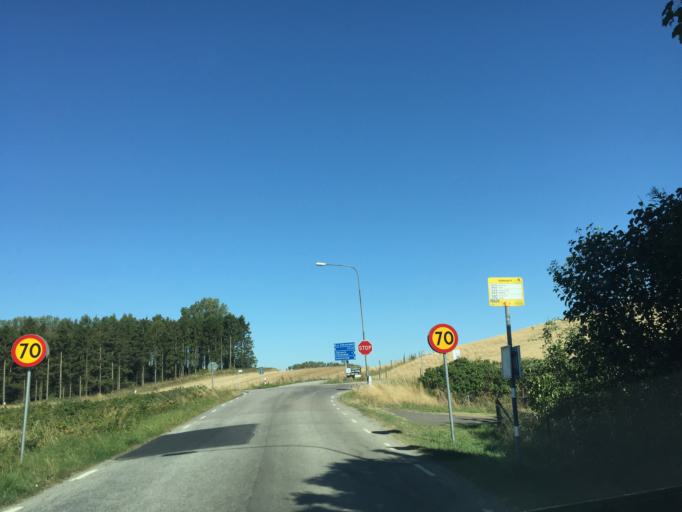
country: SE
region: Skane
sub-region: Ystads Kommun
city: Kopingebro
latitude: 55.3893
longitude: 14.0630
